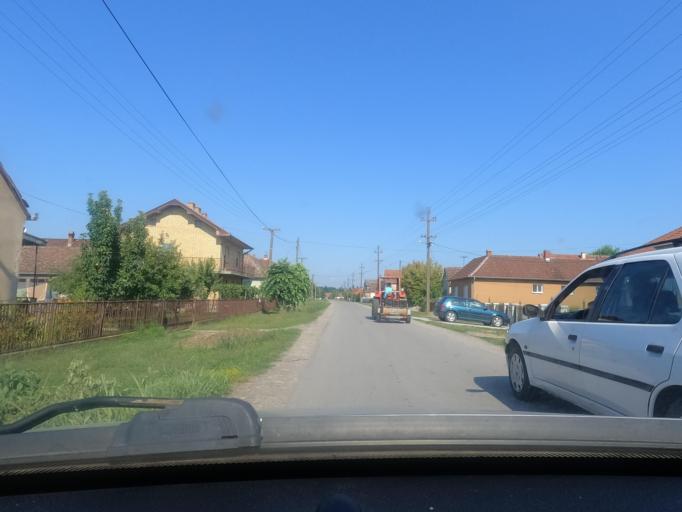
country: RS
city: Bogosavac
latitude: 44.7527
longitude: 19.5699
